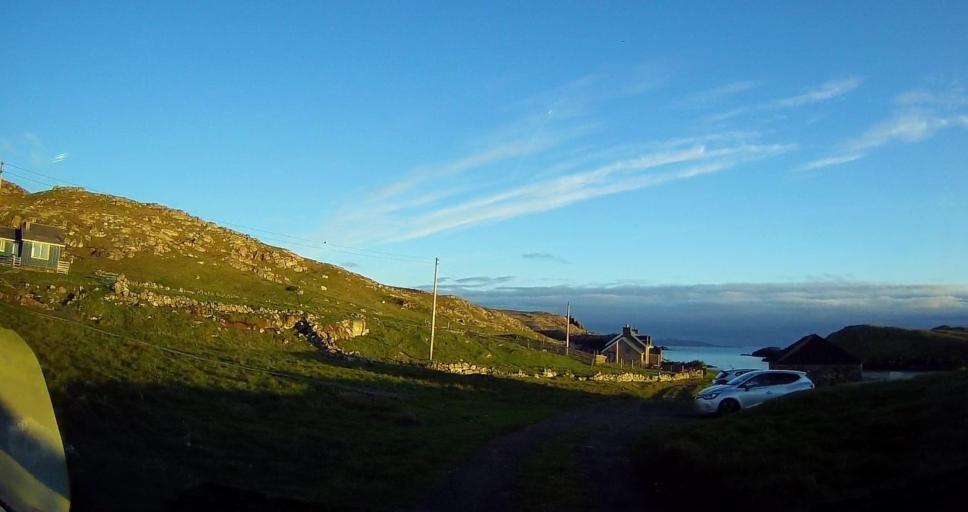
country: GB
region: Scotland
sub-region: Shetland Islands
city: Lerwick
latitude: 60.4410
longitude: -1.4478
